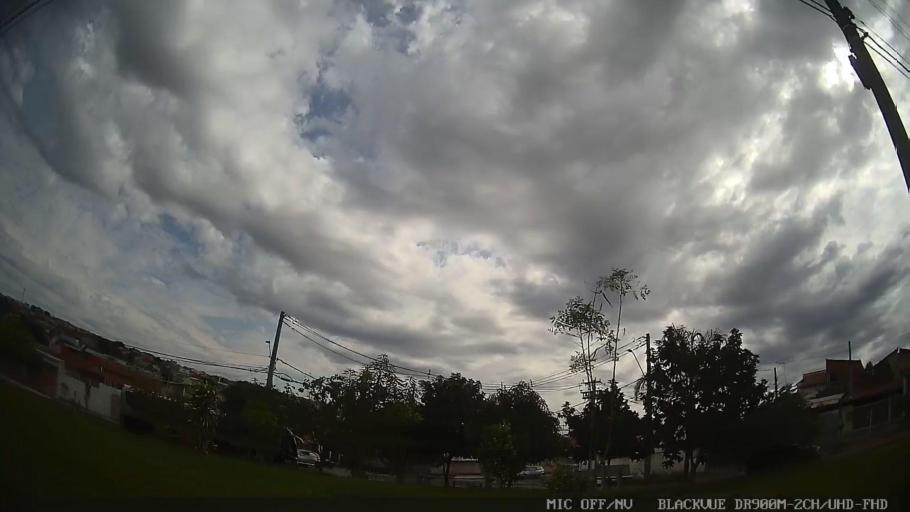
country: BR
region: Sao Paulo
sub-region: Indaiatuba
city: Indaiatuba
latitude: -23.1283
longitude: -47.2315
